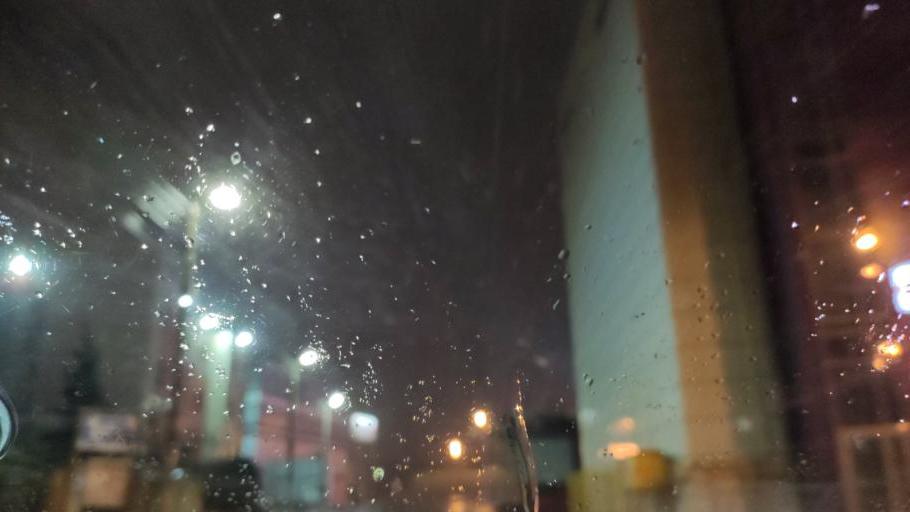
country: RU
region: Moskovskaya
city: Marfino
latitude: 55.7132
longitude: 37.3751
